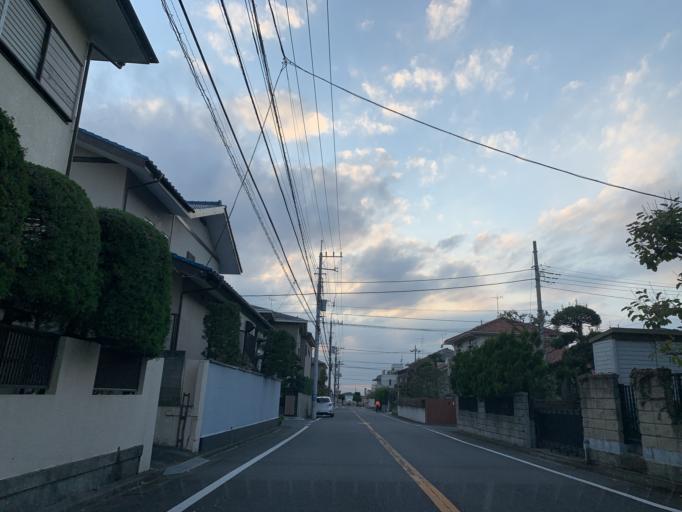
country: JP
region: Chiba
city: Nagareyama
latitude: 35.8915
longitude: 139.8991
